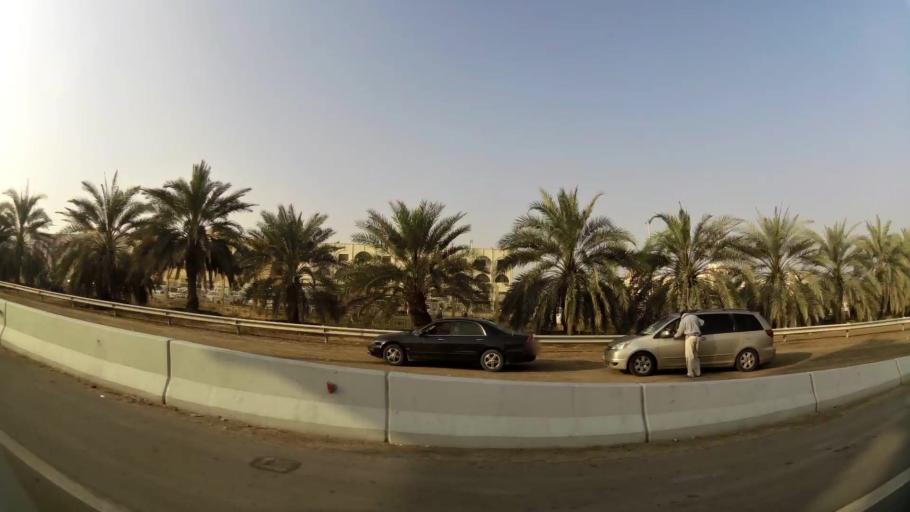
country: AE
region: Abu Dhabi
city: Abu Dhabi
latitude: 24.2831
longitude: 54.6447
